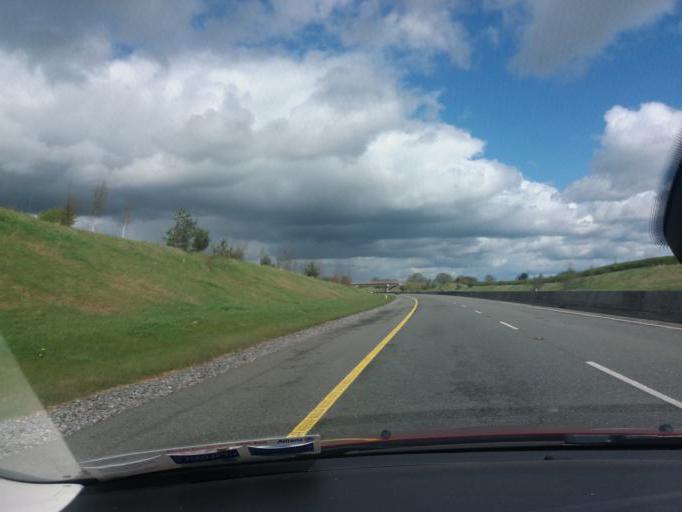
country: IE
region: Leinster
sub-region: Laois
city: Rathdowney
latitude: 52.8106
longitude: -7.4943
